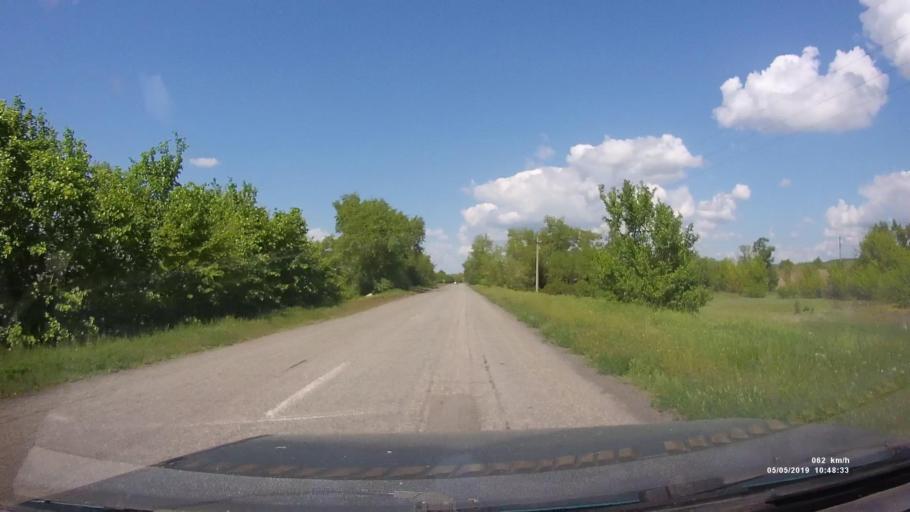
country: RU
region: Rostov
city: Ust'-Donetskiy
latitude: 47.6431
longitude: 40.8187
